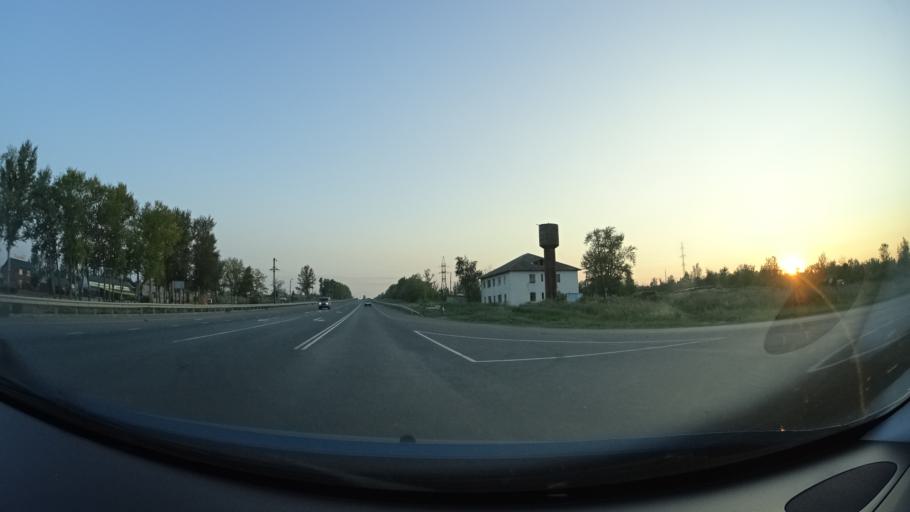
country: RU
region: Samara
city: Sukhodol
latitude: 53.8841
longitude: 51.2406
